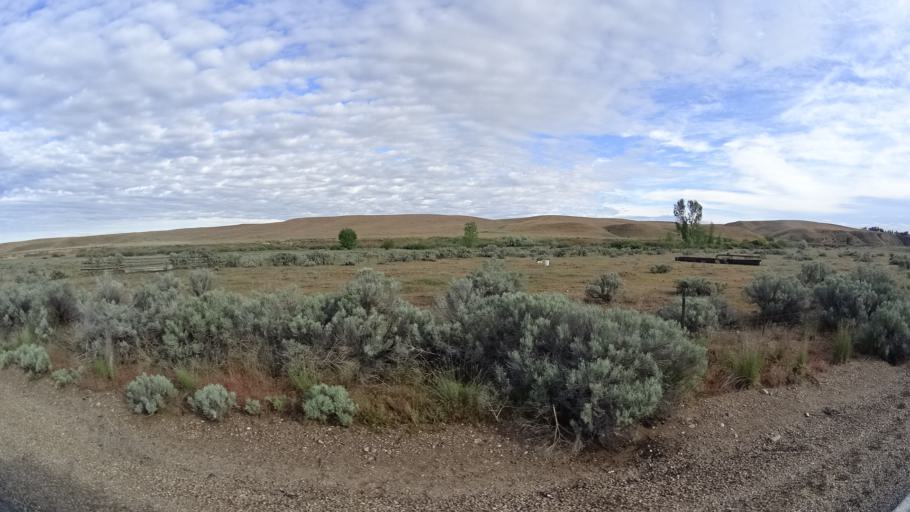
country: US
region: Idaho
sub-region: Ada County
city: Star
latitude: 43.7670
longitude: -116.4982
